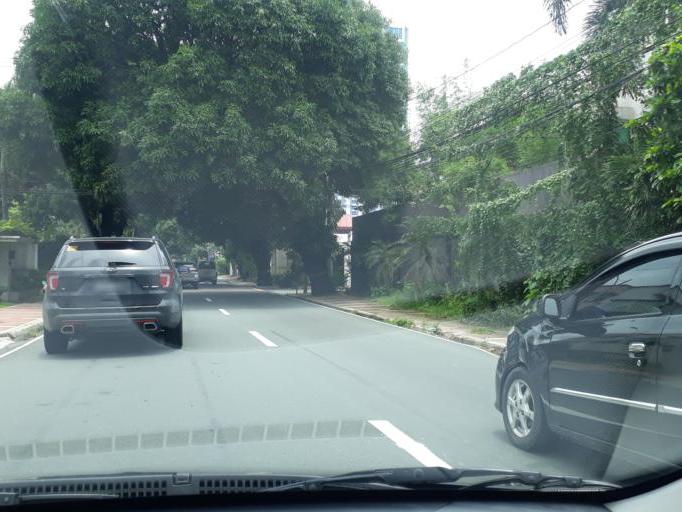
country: PH
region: Metro Manila
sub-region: San Juan
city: San Juan
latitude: 14.6166
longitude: 121.0330
